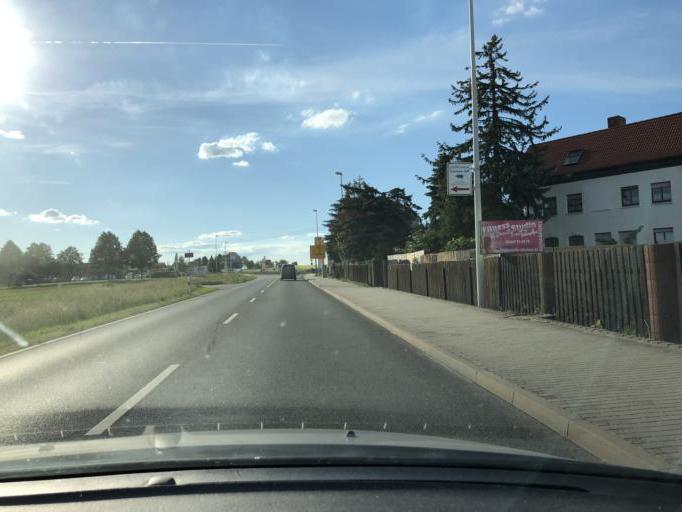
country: DE
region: Thuringia
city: Altenburg
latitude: 50.9978
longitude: 12.4114
